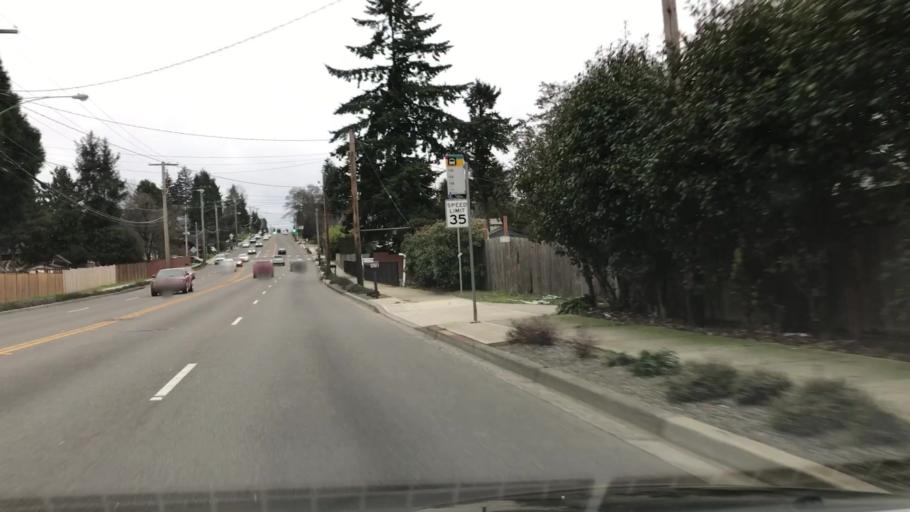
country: US
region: Washington
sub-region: King County
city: Kent
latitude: 47.3867
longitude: -122.2177
